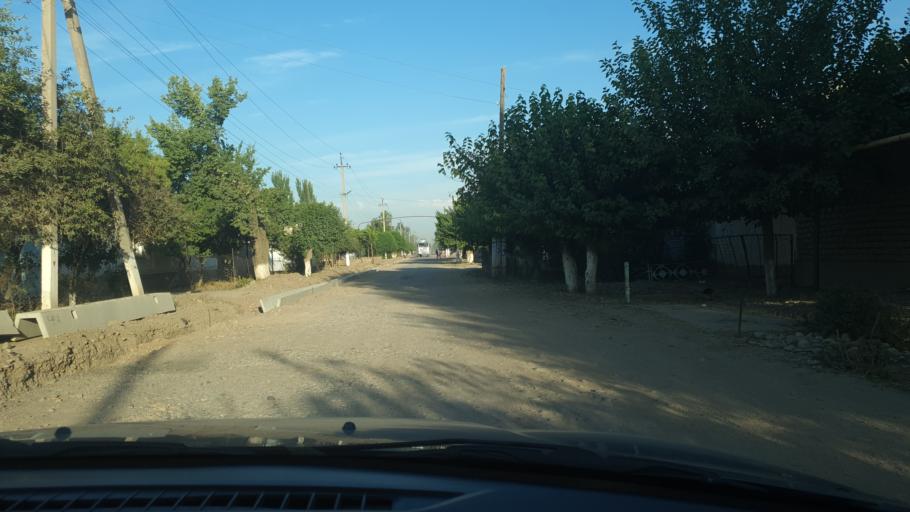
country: UZ
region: Toshkent
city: Tuytepa
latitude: 41.1053
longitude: 69.3964
